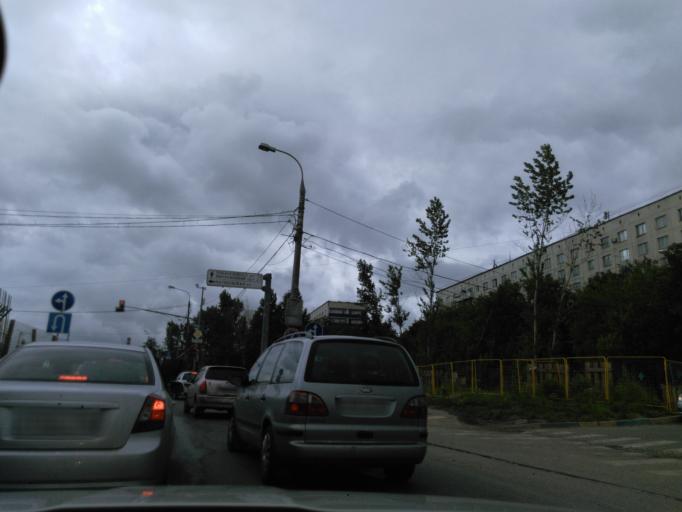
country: RU
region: Moscow
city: Amin'yevo
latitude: 55.7065
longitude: 37.4557
